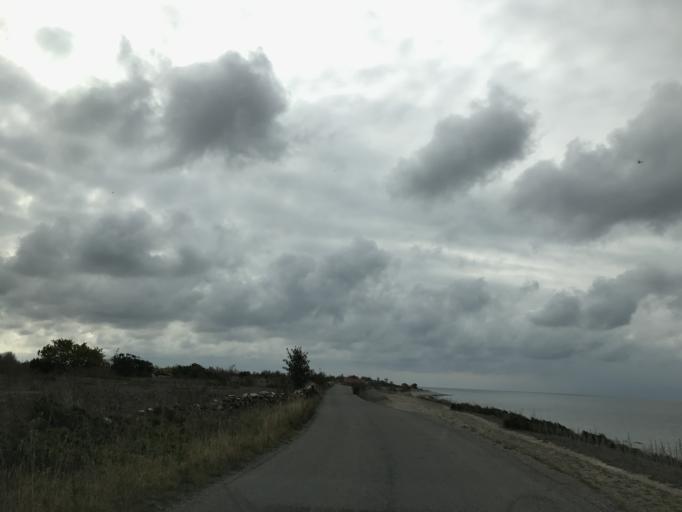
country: SE
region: Kalmar
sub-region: Borgholms Kommun
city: Borgholm
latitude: 57.0479
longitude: 16.8329
